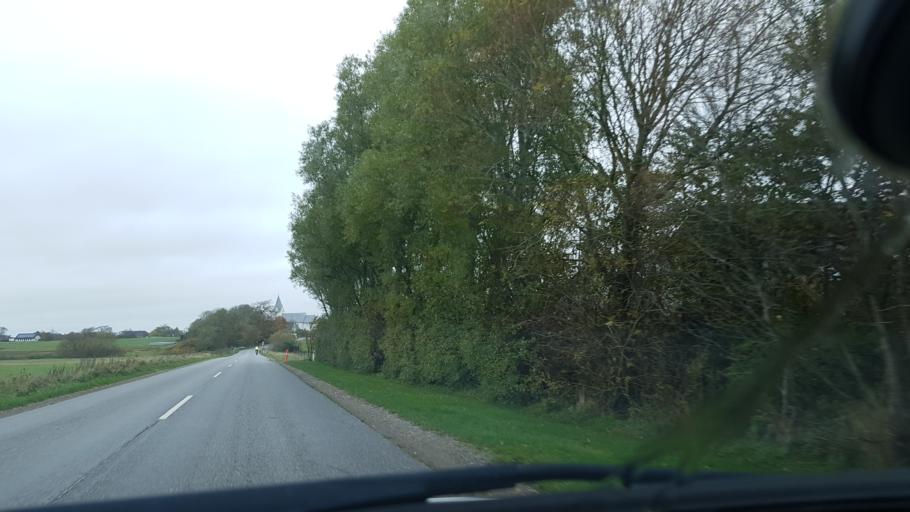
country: DK
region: South Denmark
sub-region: Tonder Kommune
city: Sherrebek
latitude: 55.2412
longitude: 8.8312
